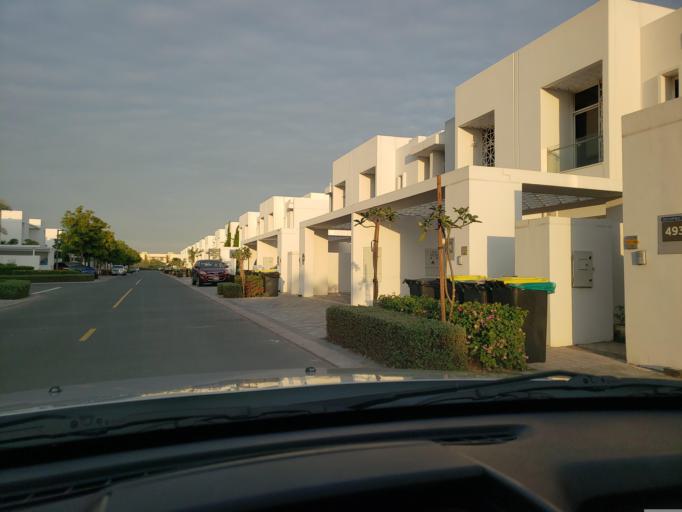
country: AE
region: Dubai
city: Dubai
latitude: 25.0166
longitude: 55.2733
